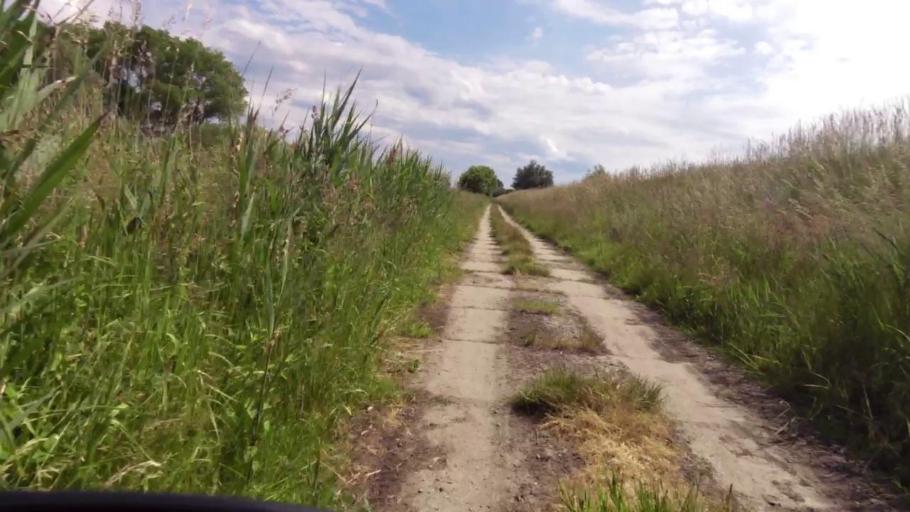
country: PL
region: West Pomeranian Voivodeship
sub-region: Powiat kamienski
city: Wolin
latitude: 53.8473
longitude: 14.5766
